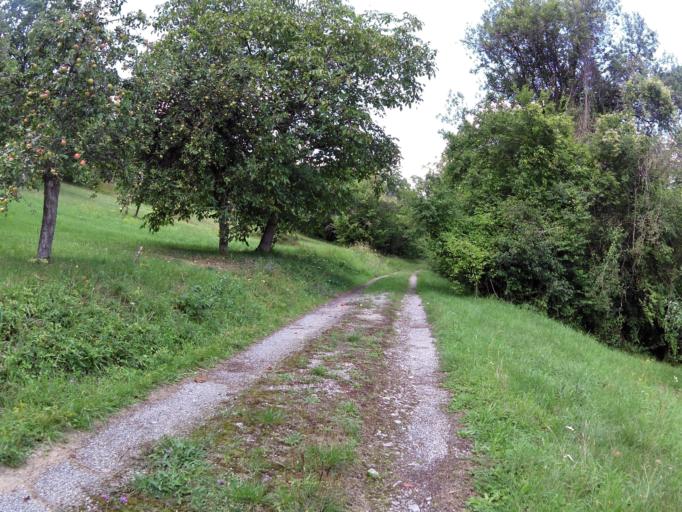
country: DE
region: Bavaria
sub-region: Regierungsbezirk Unterfranken
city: Margetshochheim
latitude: 49.8361
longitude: 9.8536
